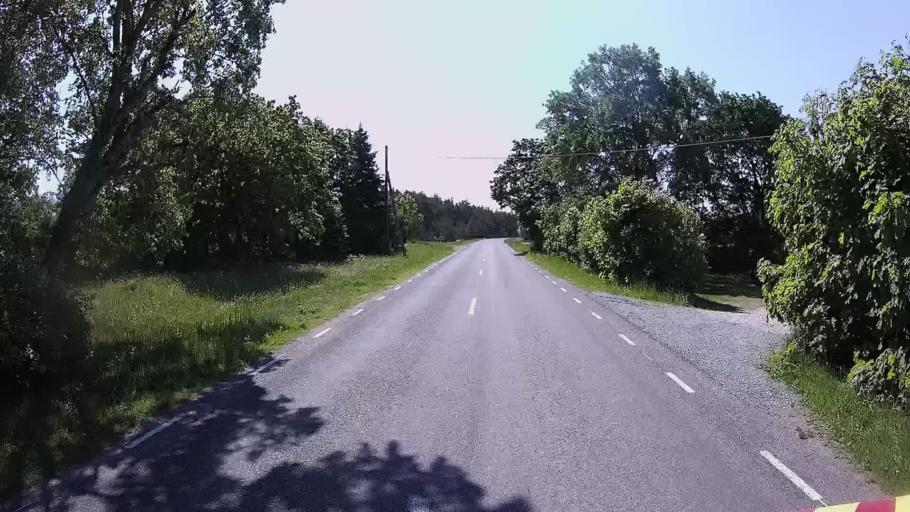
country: EE
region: Saare
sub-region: Kuressaare linn
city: Kuressaare
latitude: 58.0977
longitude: 22.2311
